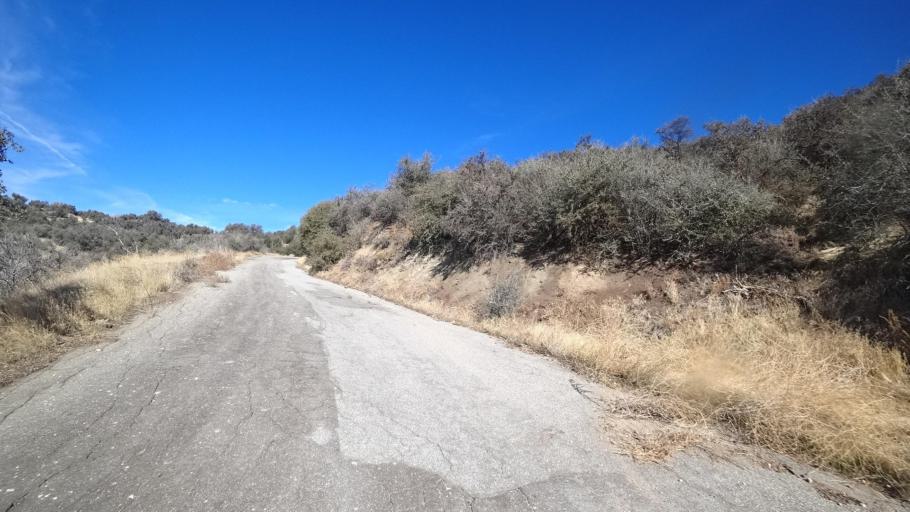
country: US
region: California
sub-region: Kern County
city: Bodfish
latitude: 35.4576
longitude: -118.6551
